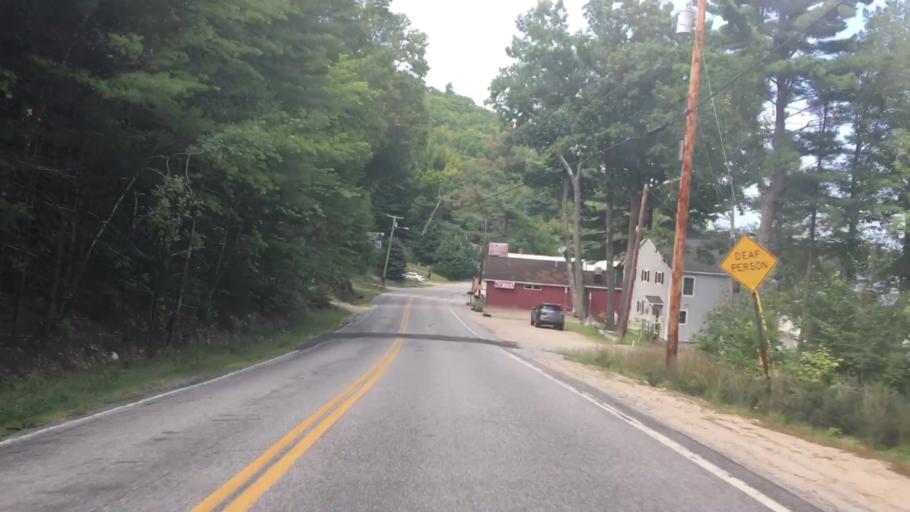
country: US
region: Maine
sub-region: Oxford County
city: Oxford
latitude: 44.1008
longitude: -70.5096
